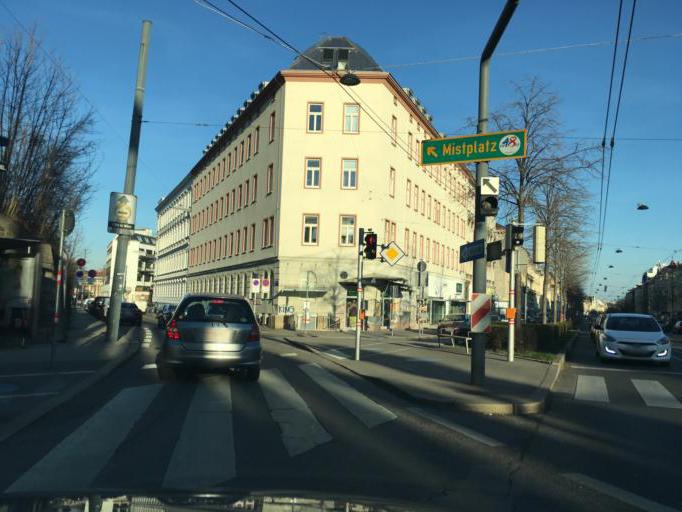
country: AT
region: Vienna
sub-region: Wien Stadt
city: Vienna
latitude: 48.2235
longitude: 16.3157
